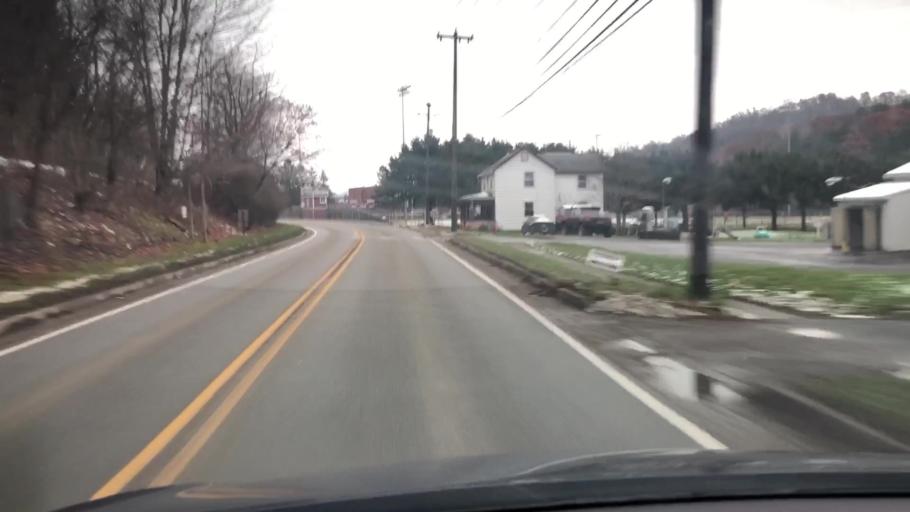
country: US
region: Pennsylvania
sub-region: Clarion County
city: Clarion
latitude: 41.0030
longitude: -79.3219
